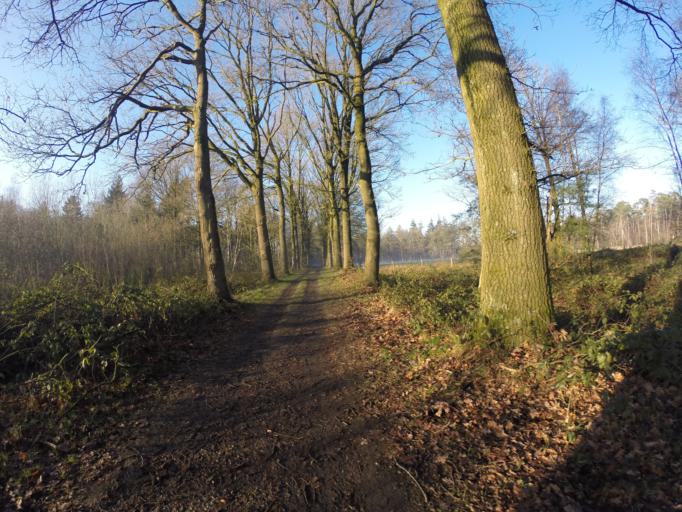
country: BE
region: Flanders
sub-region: Provincie West-Vlaanderen
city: Beernem
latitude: 51.0952
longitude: 3.3275
